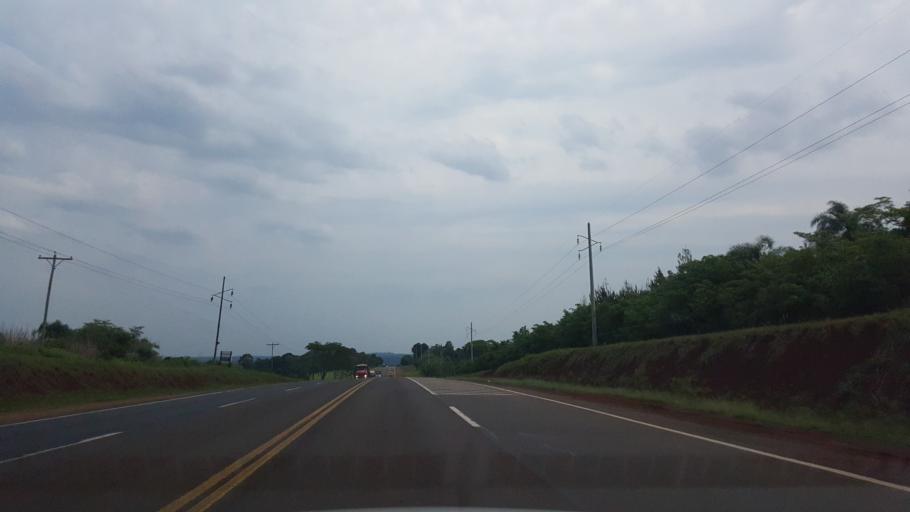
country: AR
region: Misiones
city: Capiovi
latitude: -26.9437
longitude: -55.0837
